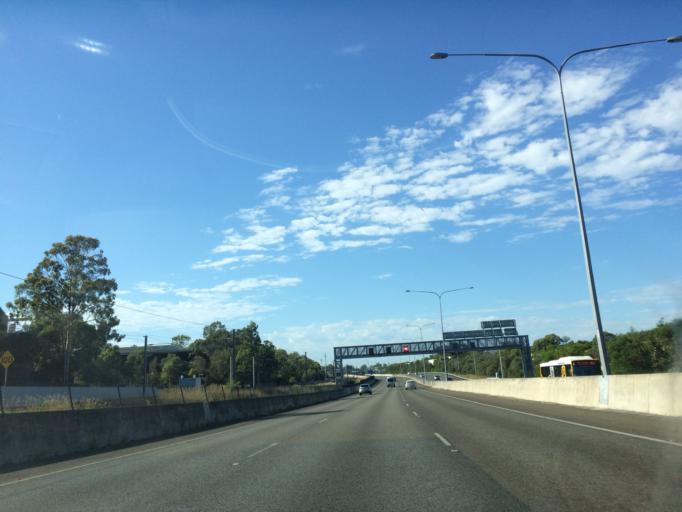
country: AU
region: Queensland
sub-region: Brisbane
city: Richlands
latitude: -27.5831
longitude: 152.9478
